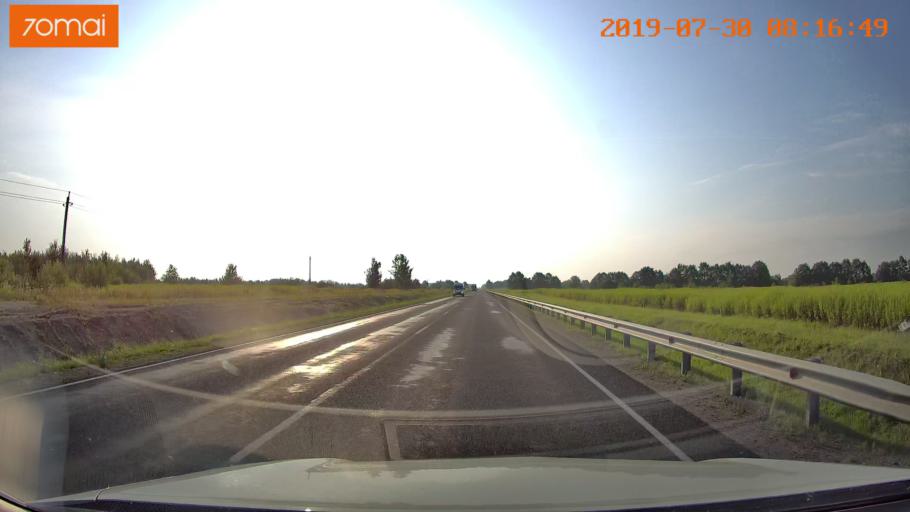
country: RU
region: Kaliningrad
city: Zheleznodorozhnyy
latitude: 54.6387
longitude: 21.4208
